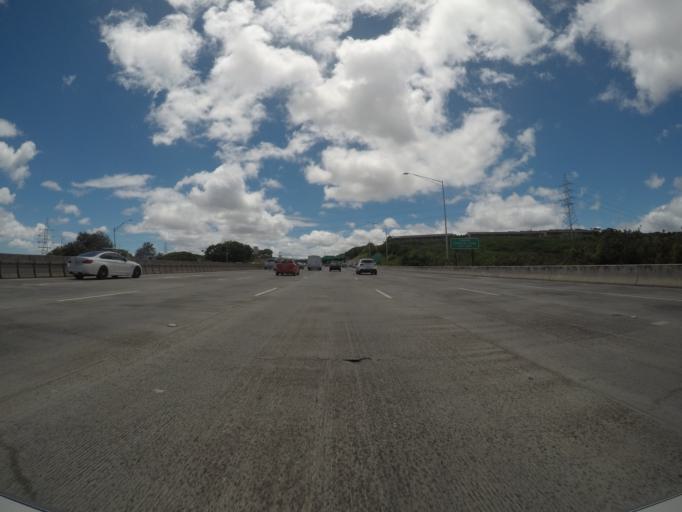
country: US
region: Hawaii
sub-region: Honolulu County
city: Waimalu
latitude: 21.3919
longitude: -157.9497
